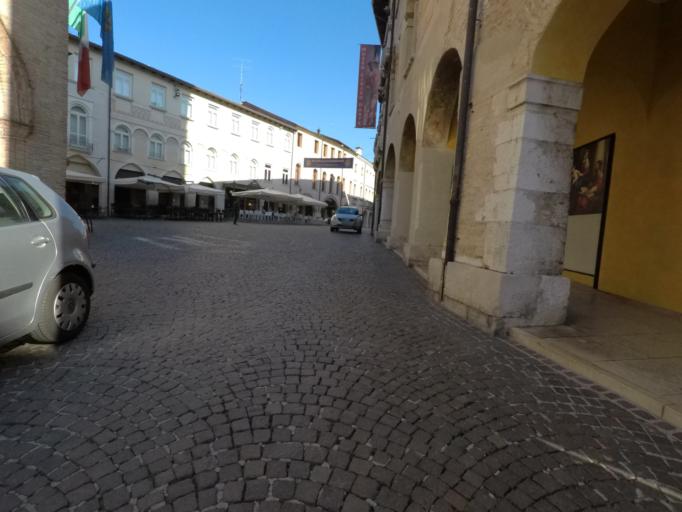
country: IT
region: Friuli Venezia Giulia
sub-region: Provincia di Pordenone
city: Pordenone
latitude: 45.9545
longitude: 12.6602
